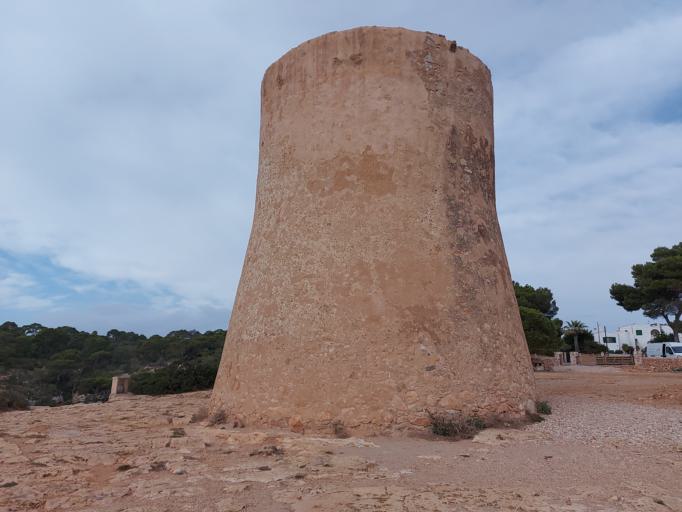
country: ES
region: Balearic Islands
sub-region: Illes Balears
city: Llucmajor
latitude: 39.3614
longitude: 2.8354
